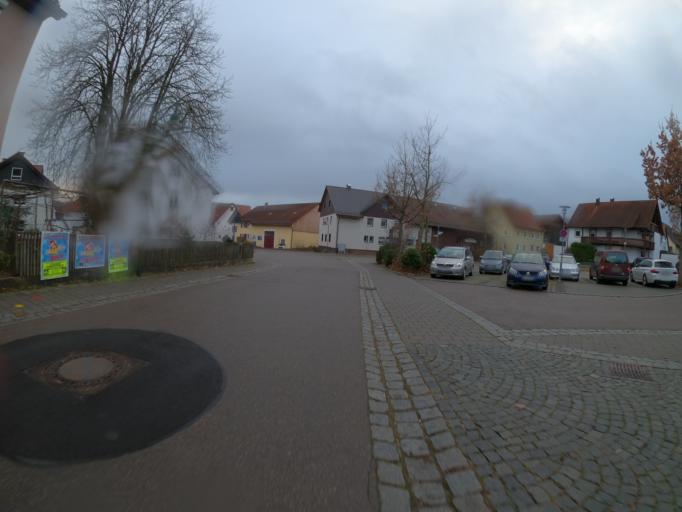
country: DE
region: Baden-Wuerttemberg
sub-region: Regierungsbezirk Stuttgart
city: Waschenbeuren
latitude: 48.7609
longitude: 9.6845
